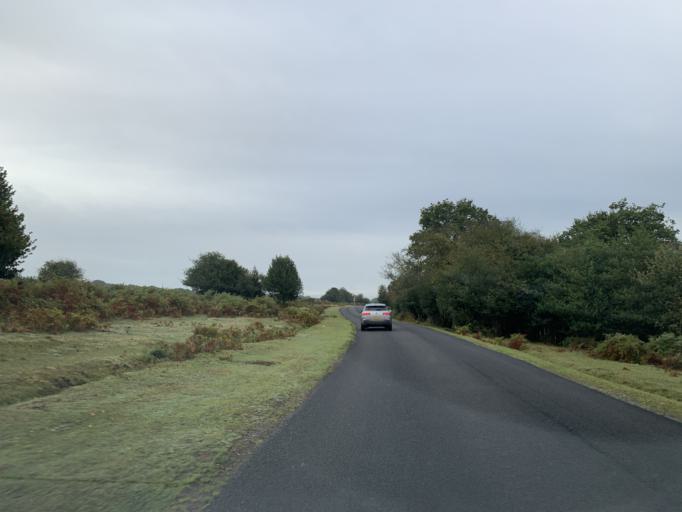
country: GB
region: England
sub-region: Wiltshire
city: Whiteparish
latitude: 50.9417
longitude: -1.6509
